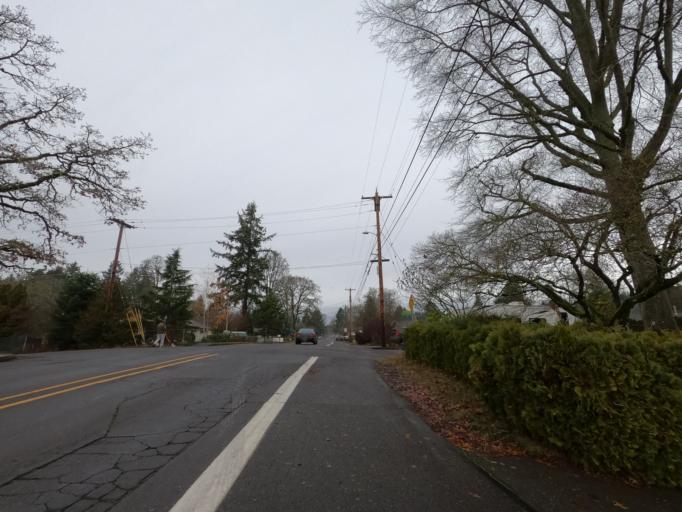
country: US
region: Oregon
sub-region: Clackamas County
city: Gladstone
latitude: 45.3894
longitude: -122.6007
